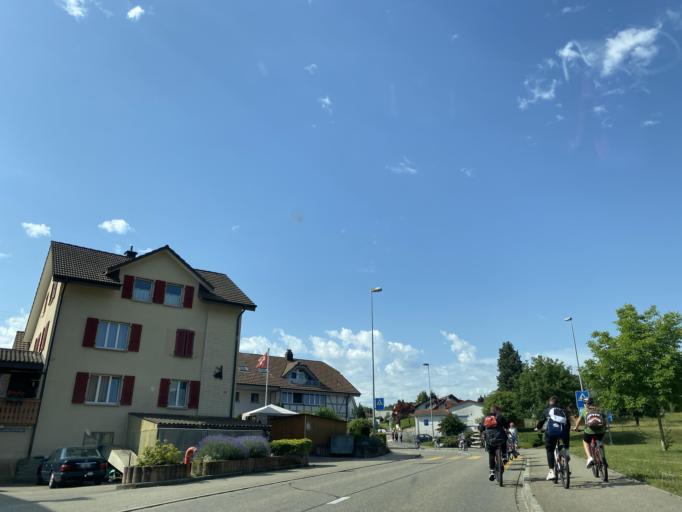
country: CH
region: Aargau
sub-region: Bezirk Zofingen
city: Rothrist
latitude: 47.3042
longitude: 7.8874
